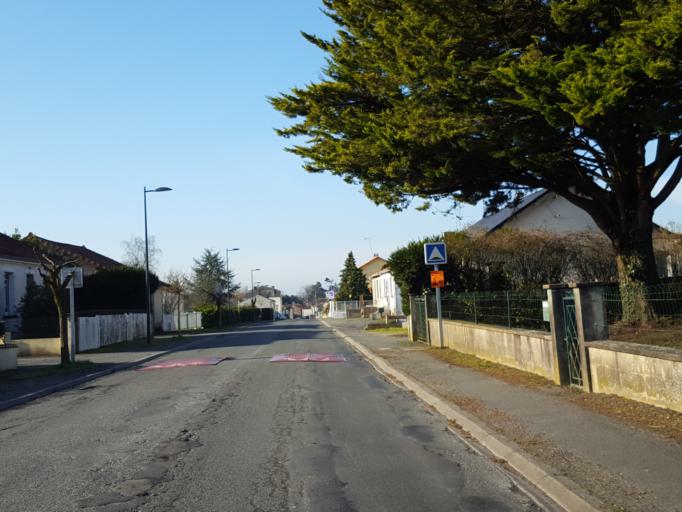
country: FR
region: Pays de la Loire
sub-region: Departement de la Vendee
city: La Chaize-le-Vicomte
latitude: 46.6751
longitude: -1.2882
